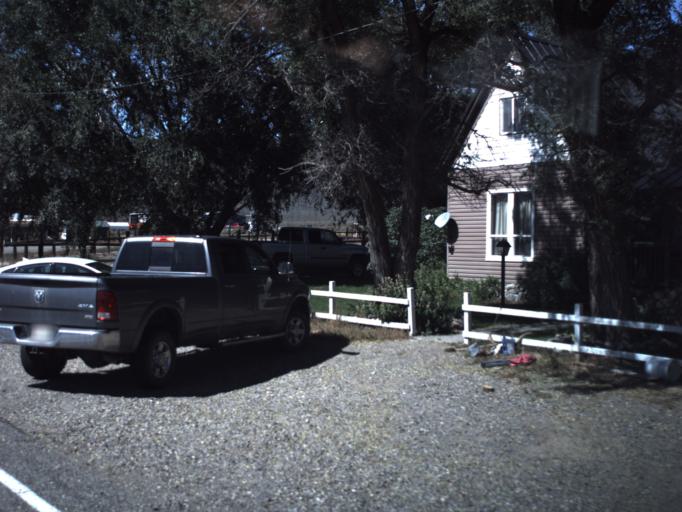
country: US
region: Utah
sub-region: Piute County
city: Junction
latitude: 38.2369
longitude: -112.2251
